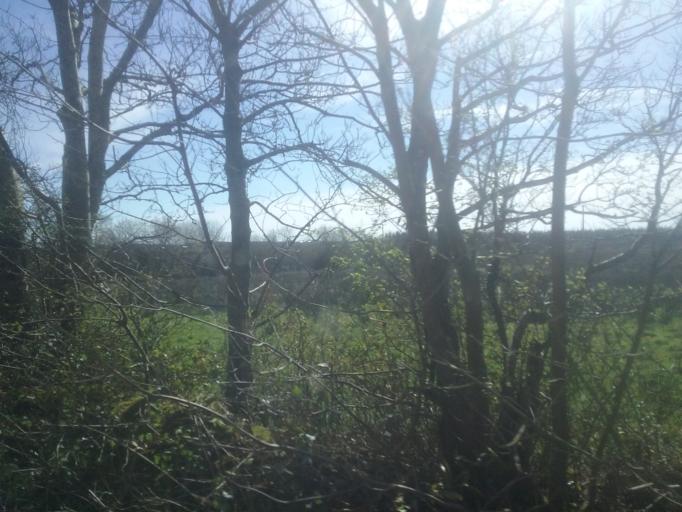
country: IE
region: Munster
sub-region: An Clar
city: Kilrush
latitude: 52.6698
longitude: -9.5214
